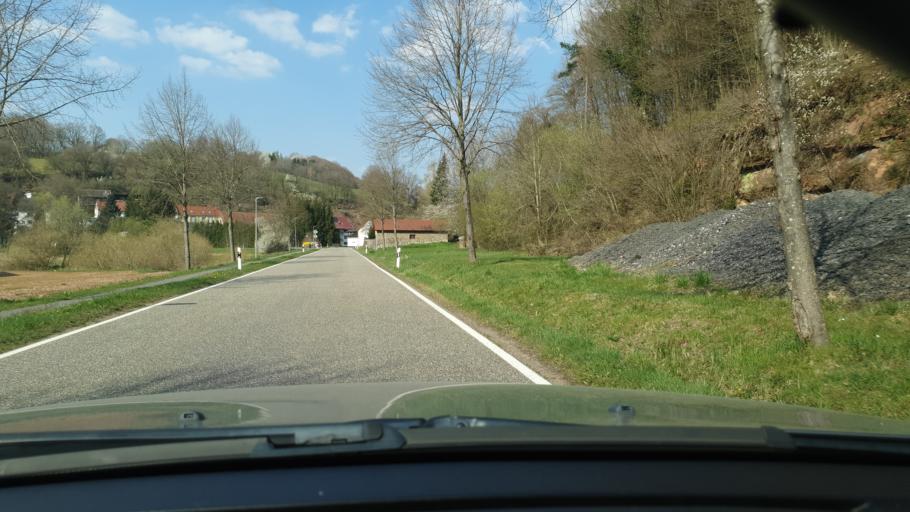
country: DE
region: Rheinland-Pfalz
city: Battweiler
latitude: 49.2994
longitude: 7.4683
